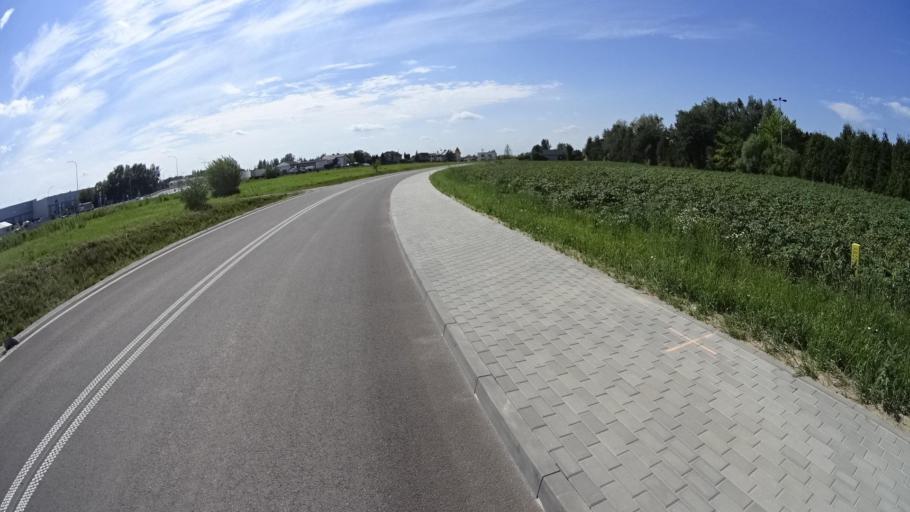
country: PL
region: Masovian Voivodeship
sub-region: Powiat piaseczynski
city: Mysiadlo
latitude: 52.1184
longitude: 20.9832
